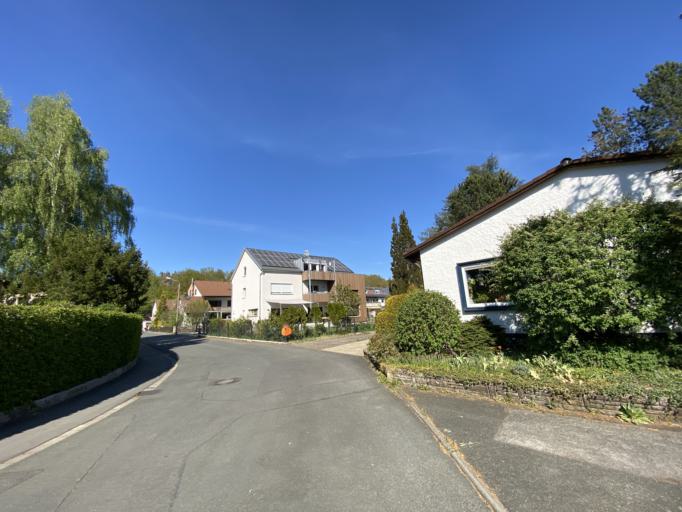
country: DE
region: Bavaria
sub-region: Regierungsbezirk Mittelfranken
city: Buckenhof
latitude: 49.5970
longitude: 11.0458
